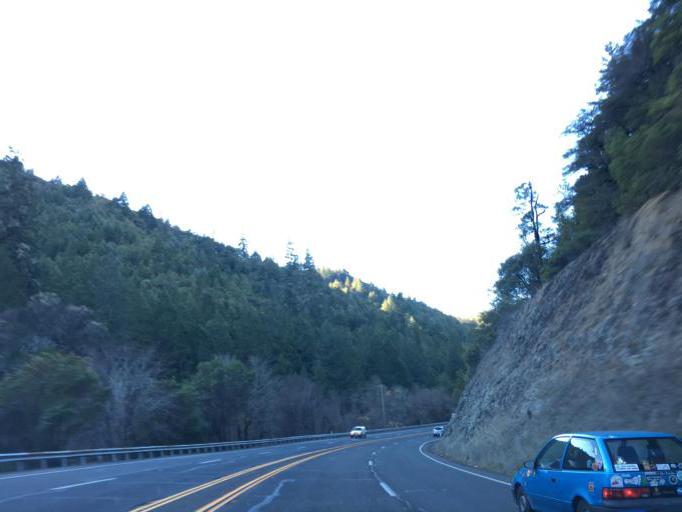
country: US
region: California
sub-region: Mendocino County
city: Brooktrails
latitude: 39.5346
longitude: -123.4120
